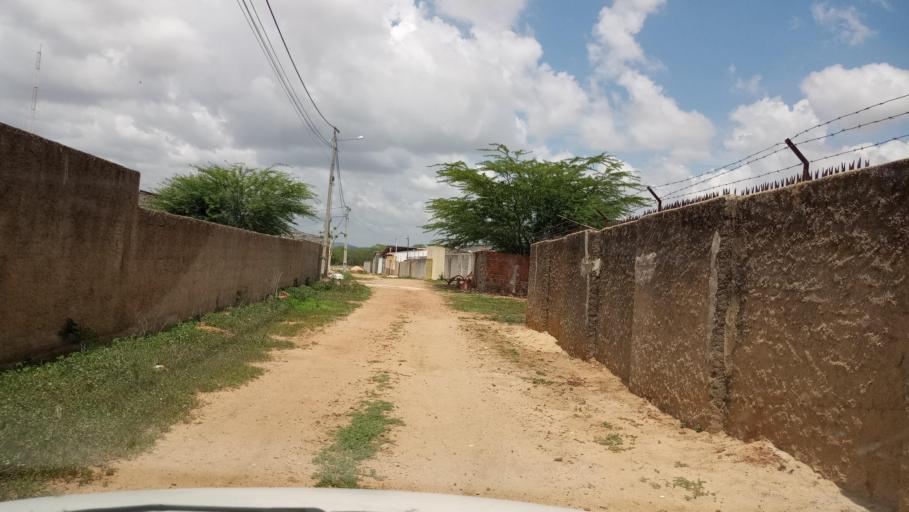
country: BR
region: Rio Grande do Norte
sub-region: Tangara
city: Tangara
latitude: -6.1071
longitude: -35.7139
